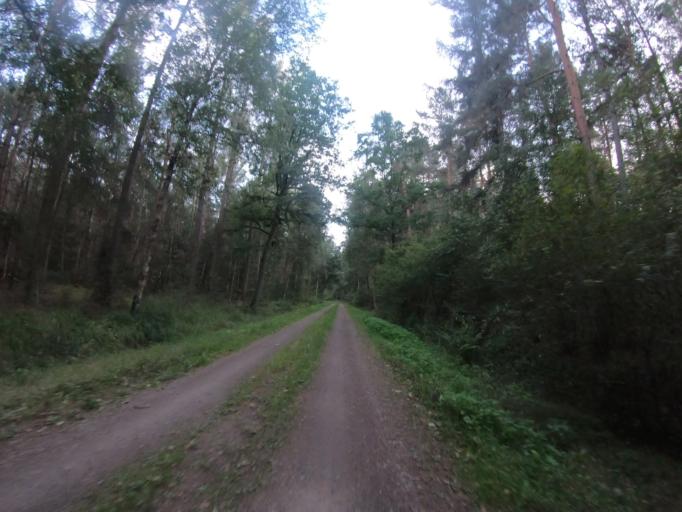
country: DE
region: Lower Saxony
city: Gifhorn
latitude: 52.5129
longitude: 10.5608
